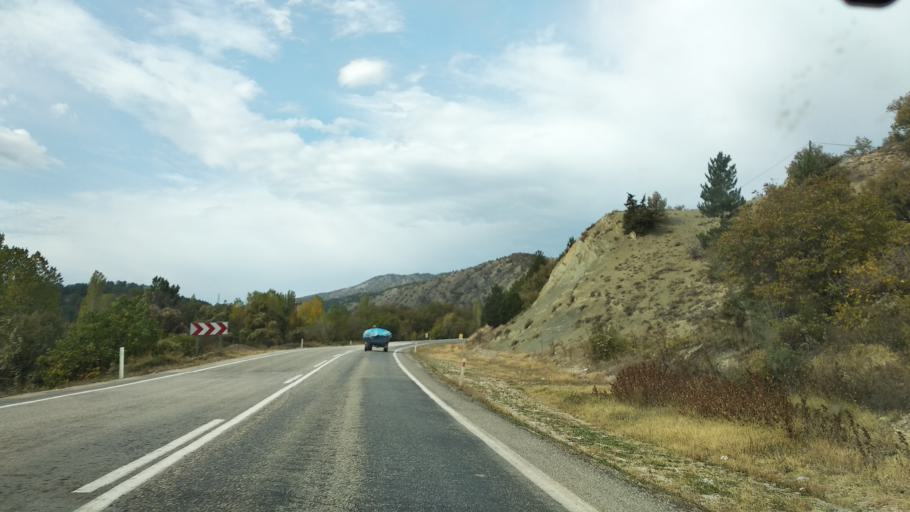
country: TR
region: Ankara
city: Nallihan
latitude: 40.3085
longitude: 31.2726
